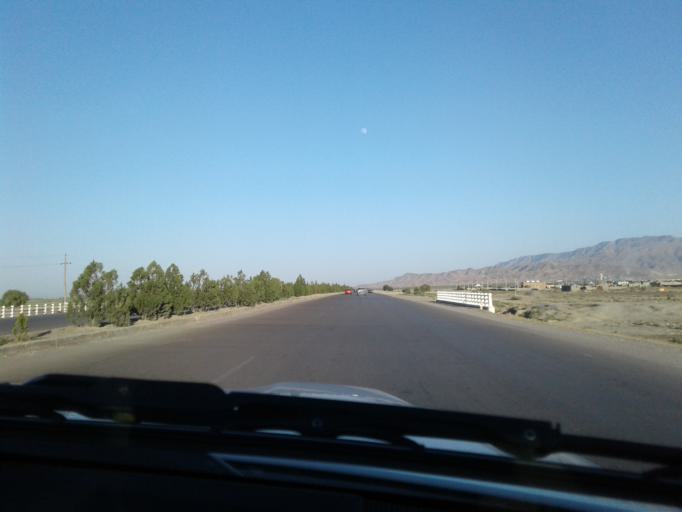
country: TM
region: Ahal
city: Baharly
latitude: 38.3082
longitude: 57.6178
